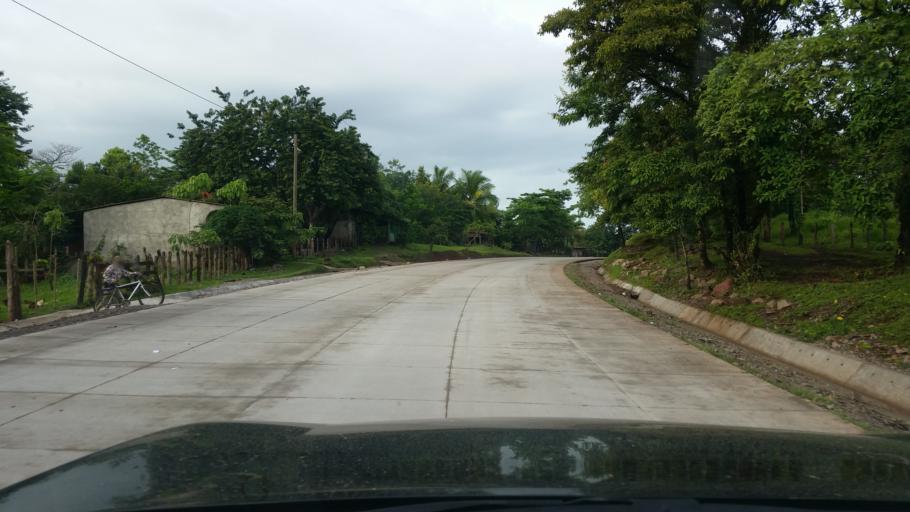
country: NI
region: Matagalpa
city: Rio Blanco
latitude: 13.1195
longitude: -85.0592
